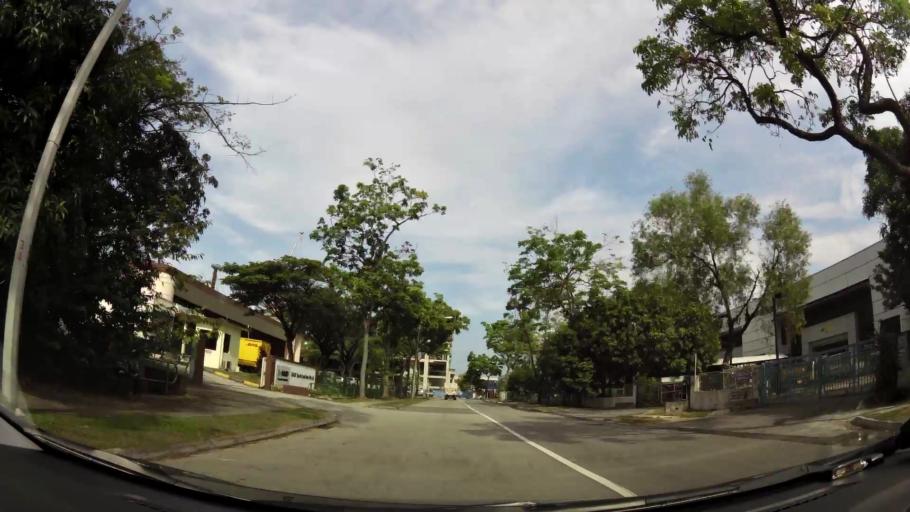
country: MY
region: Johor
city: Johor Bahru
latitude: 1.3271
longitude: 103.6397
